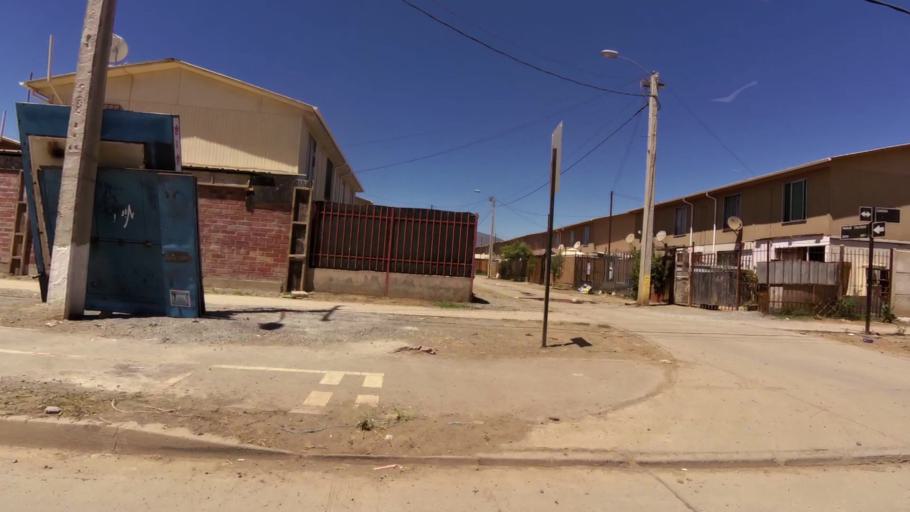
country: CL
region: O'Higgins
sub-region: Provincia de Cachapoal
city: Machali
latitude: -34.1595
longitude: -70.6947
